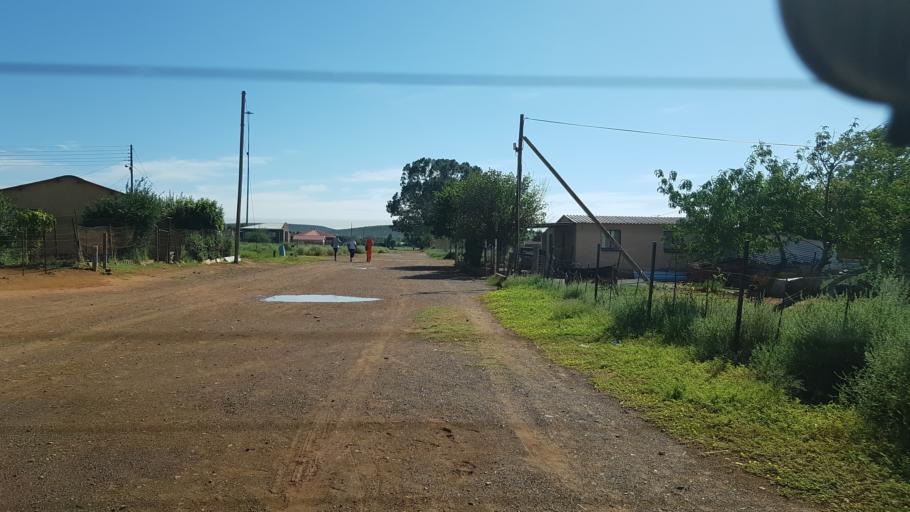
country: ZA
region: Northern Cape
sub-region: Siyanda District Municipality
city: Danielskuil
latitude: -28.1920
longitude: 23.5366
